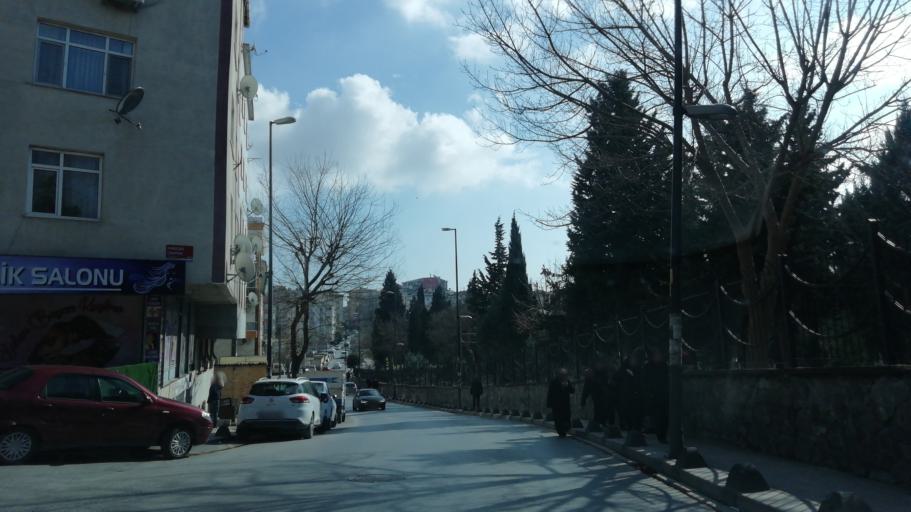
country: TR
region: Istanbul
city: Bahcelievler
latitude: 41.0160
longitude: 28.8379
